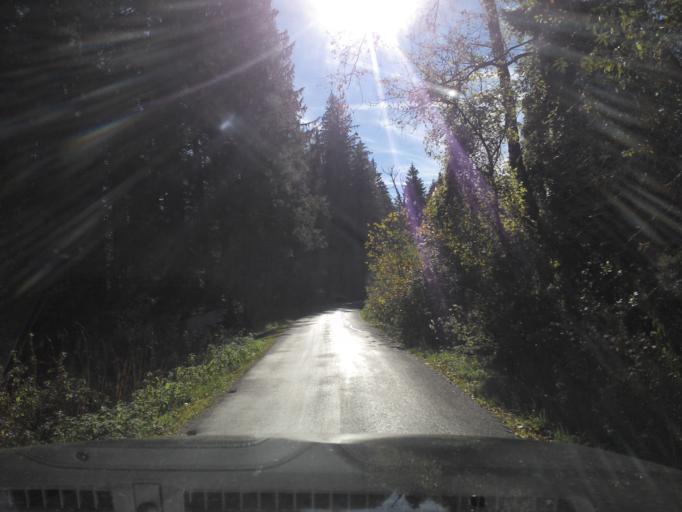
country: DE
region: Bavaria
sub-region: Upper Bavaria
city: Iffeldorf
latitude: 47.8005
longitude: 11.3405
